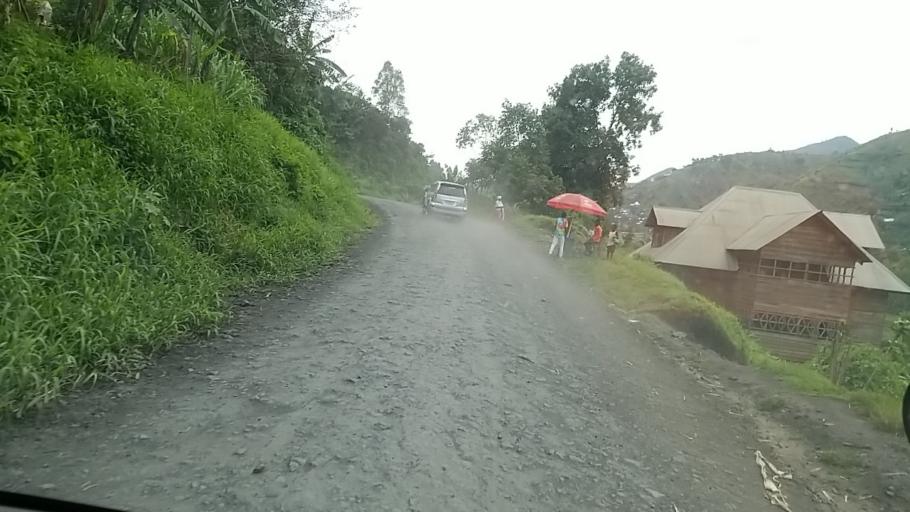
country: CD
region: Nord Kivu
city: Sake
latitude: -1.7469
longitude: 28.9886
